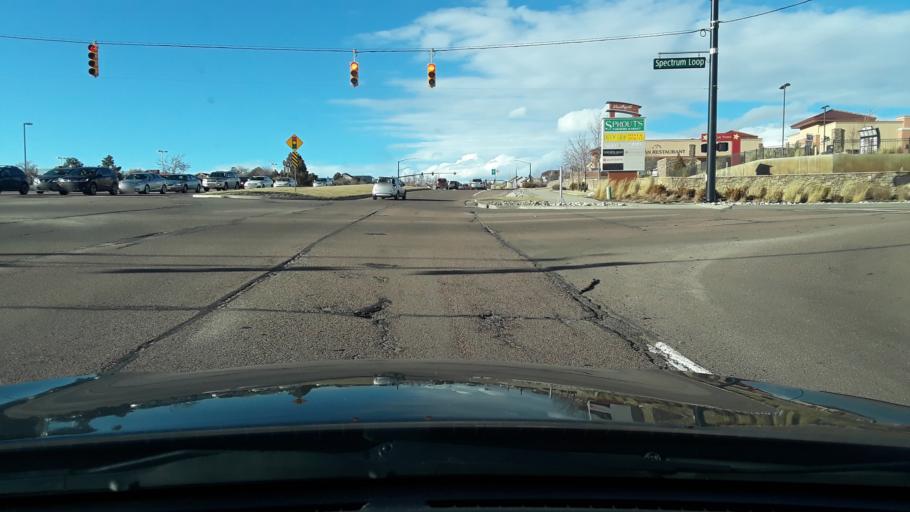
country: US
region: Colorado
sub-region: El Paso County
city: Gleneagle
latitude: 39.0248
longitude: -104.8170
